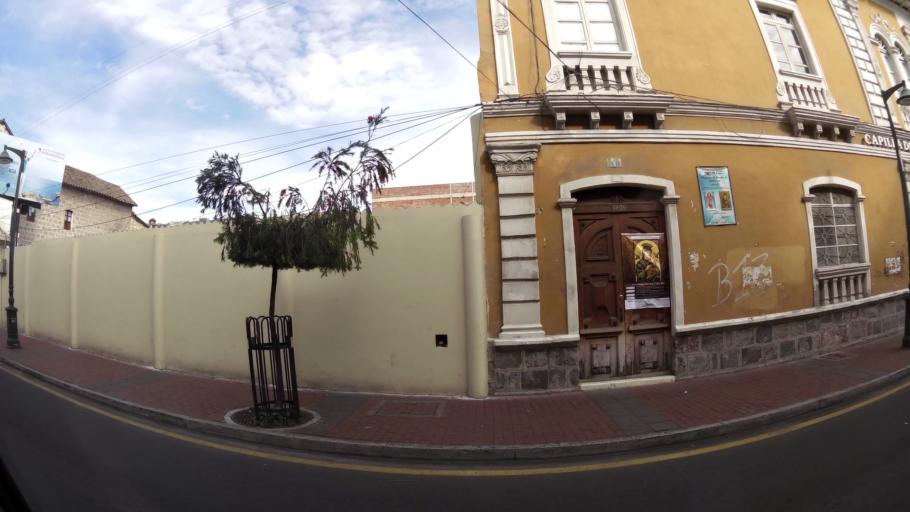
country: EC
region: Tungurahua
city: Ambato
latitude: -1.2456
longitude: -78.6291
